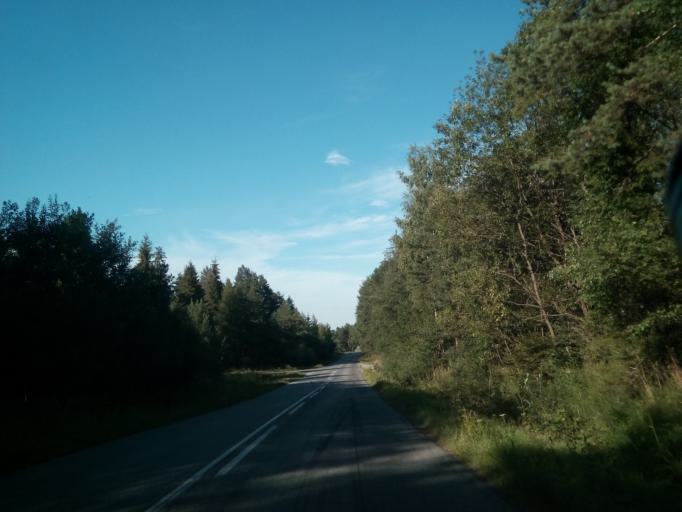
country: SK
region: Presovsky
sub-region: Okres Poprad
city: Svit
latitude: 49.0224
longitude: 20.2496
